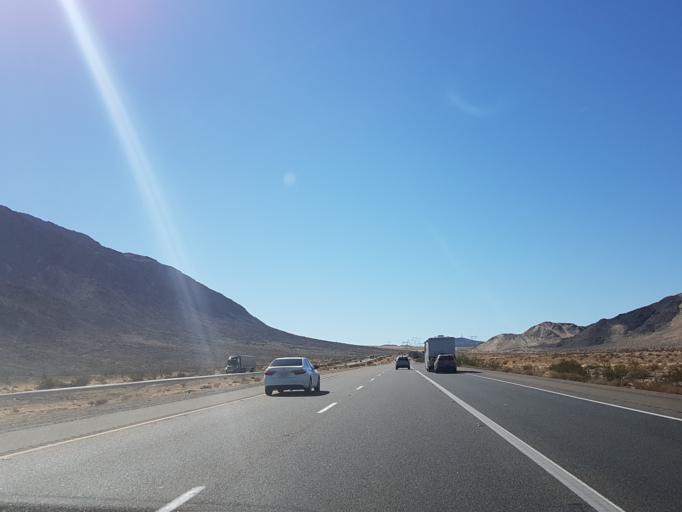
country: US
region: California
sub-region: San Bernardino County
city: Fort Irwin
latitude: 35.0947
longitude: -116.3029
